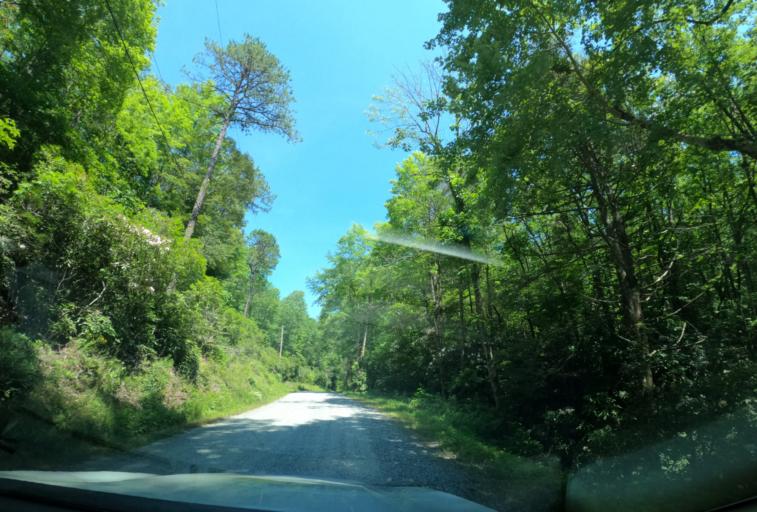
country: US
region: North Carolina
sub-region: Transylvania County
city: Brevard
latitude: 35.1844
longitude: -82.6465
